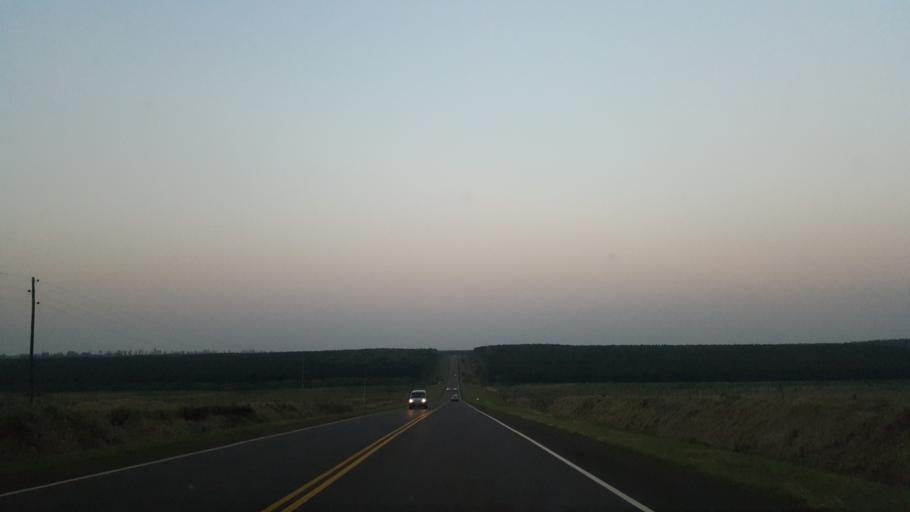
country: AR
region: Misiones
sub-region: Departamento de Capital
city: Posadas
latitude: -27.4415
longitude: -56.0250
